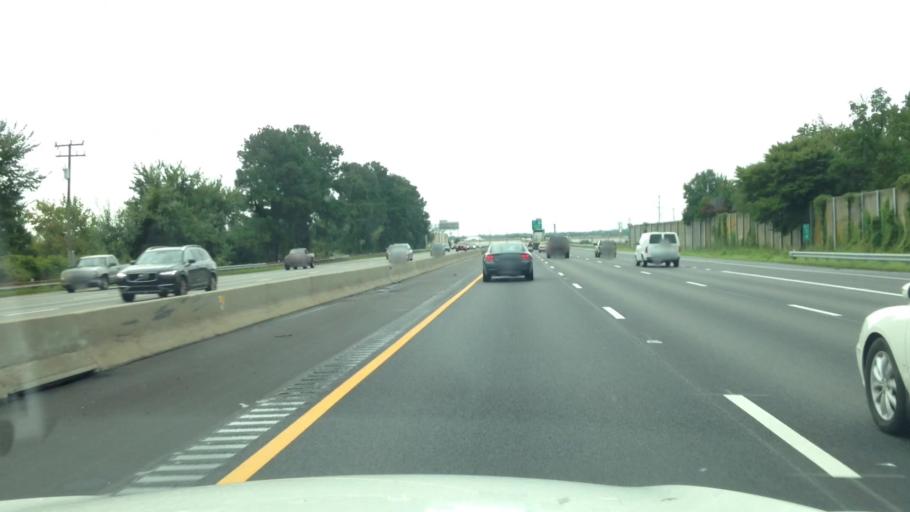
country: US
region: Virginia
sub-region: City of Colonial Heights
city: Colonial Heights
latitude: 37.2536
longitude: -77.3965
